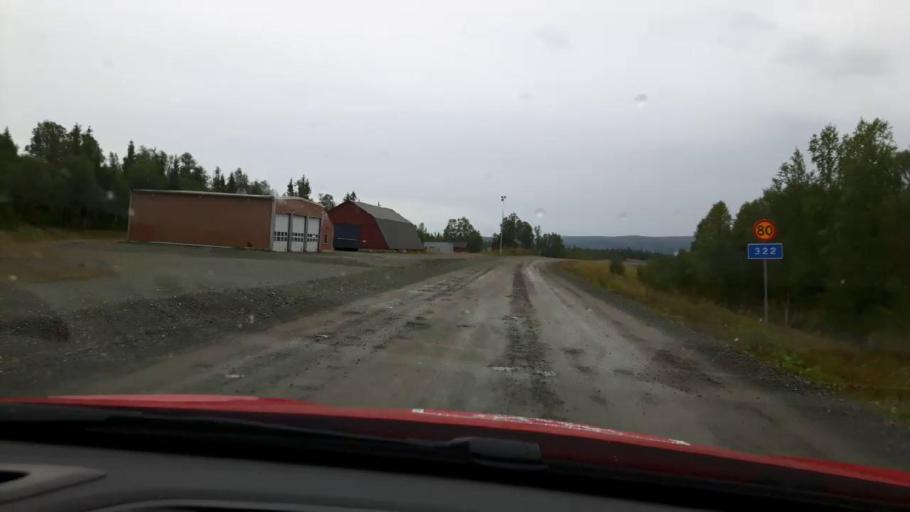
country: NO
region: Nord-Trondelag
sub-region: Meraker
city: Meraker
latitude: 63.5691
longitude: 12.2851
